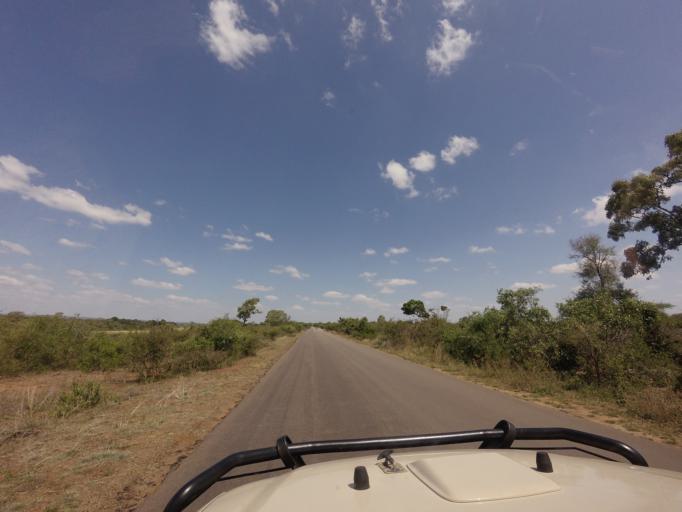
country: ZA
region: Mpumalanga
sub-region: Ehlanzeni District
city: Komatipoort
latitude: -25.1145
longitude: 31.9105
